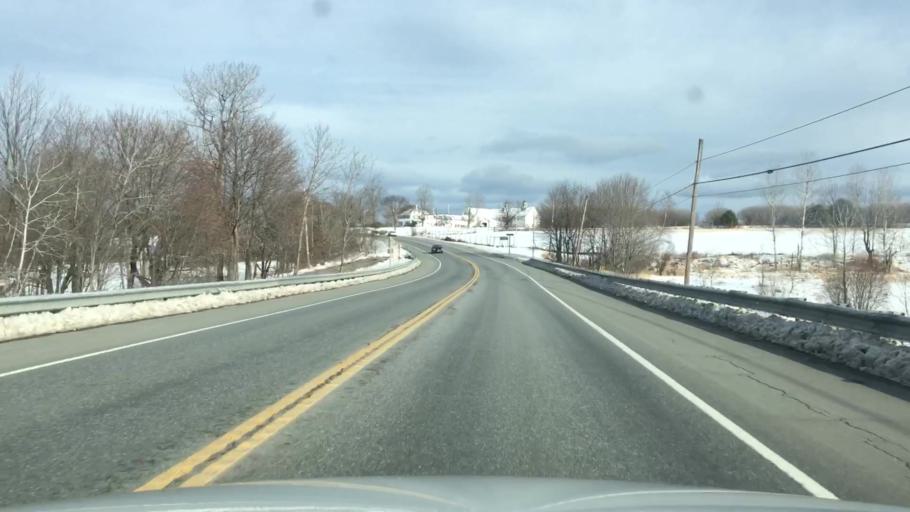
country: US
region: Maine
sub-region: Kennebec County
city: Monmouth
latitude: 44.2303
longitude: -70.0751
